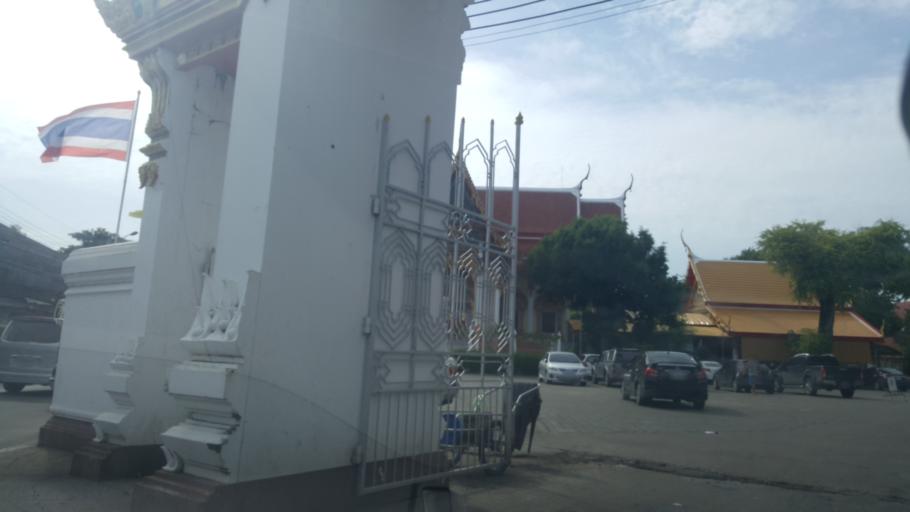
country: TH
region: Chon Buri
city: Sattahip
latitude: 12.6626
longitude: 100.8995
